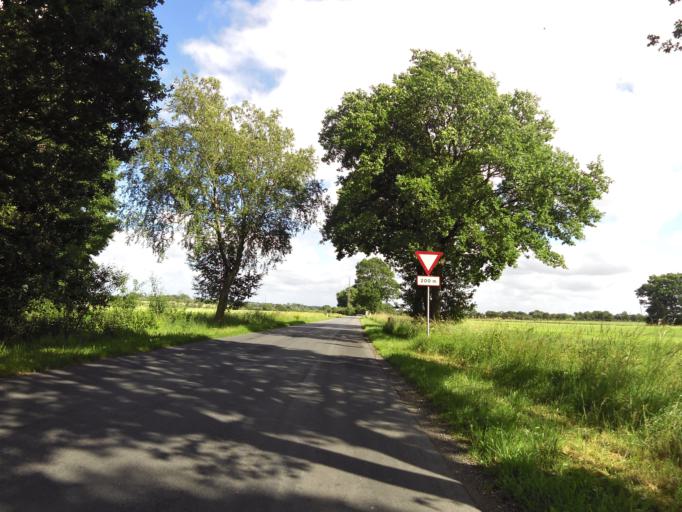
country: DK
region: South Denmark
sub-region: Kolding Kommune
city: Vamdrup
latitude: 55.3514
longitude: 9.2264
